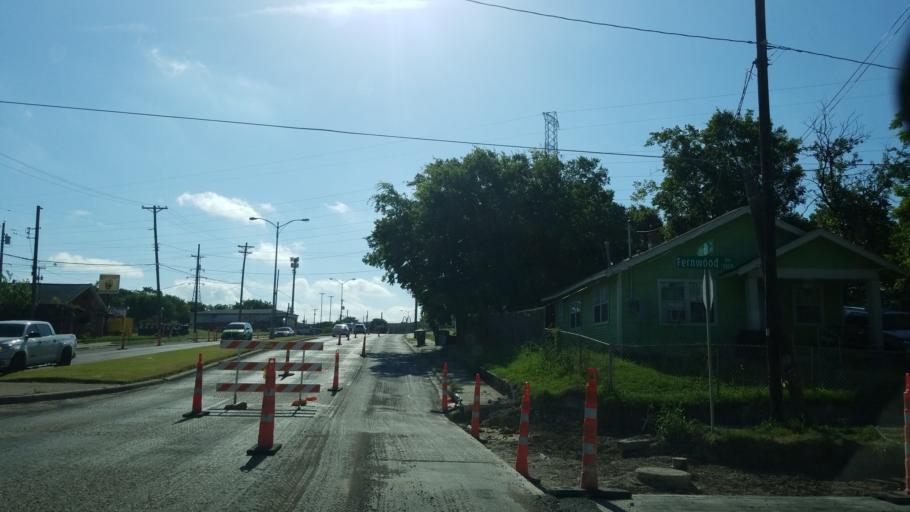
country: US
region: Texas
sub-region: Dallas County
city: Dallas
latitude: 32.7202
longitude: -96.8086
